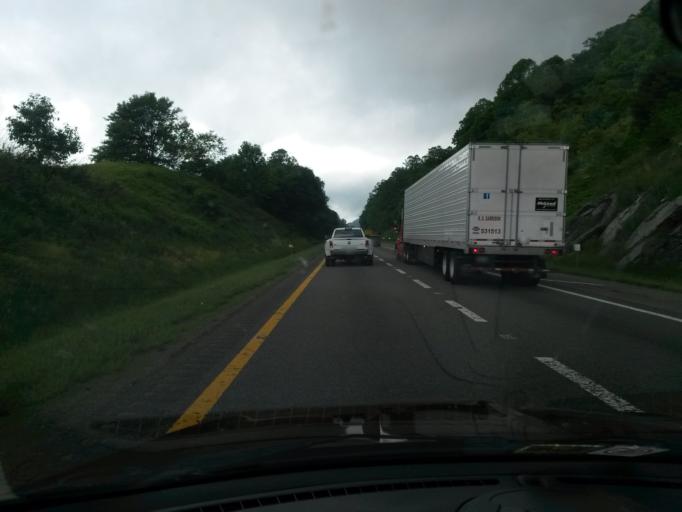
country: US
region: Virginia
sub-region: Carroll County
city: Cana
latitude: 36.6407
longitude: -80.7167
